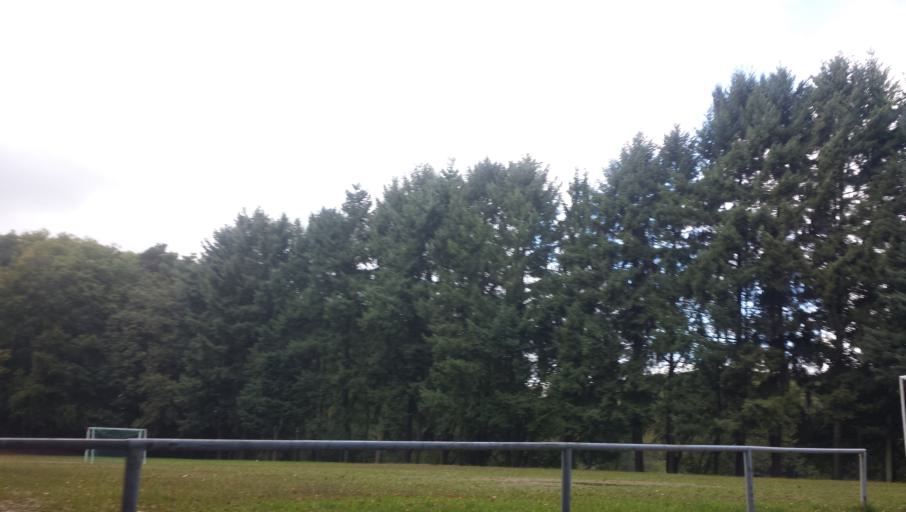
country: DE
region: Hesse
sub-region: Regierungsbezirk Darmstadt
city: Birkenau
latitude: 49.5124
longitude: 8.7203
